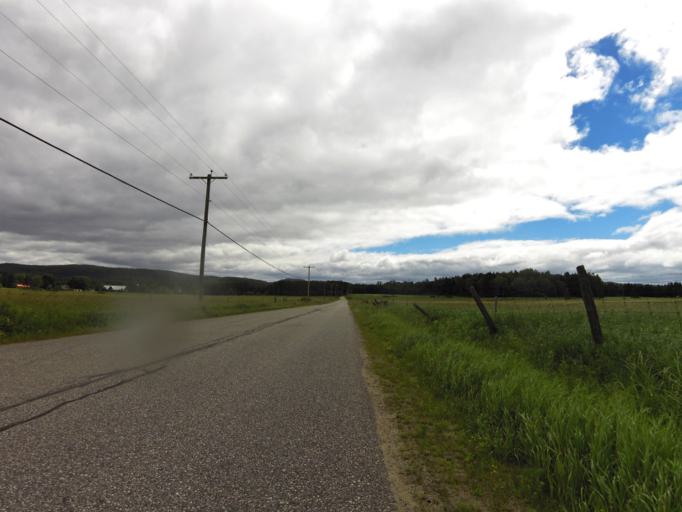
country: CA
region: Quebec
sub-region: Laurentides
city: Mont-Tremblant
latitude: 45.9567
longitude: -74.5959
